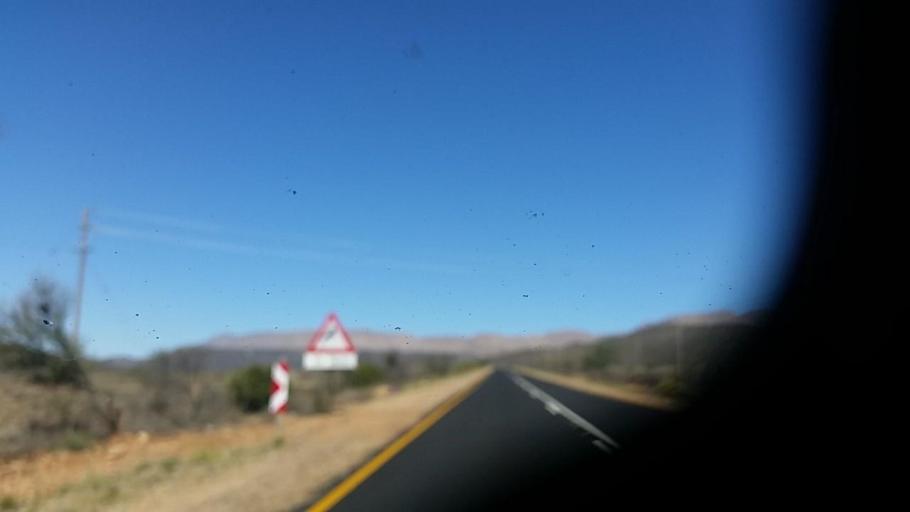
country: ZA
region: Western Cape
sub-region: Eden District Municipality
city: George
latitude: -33.5373
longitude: 22.7203
